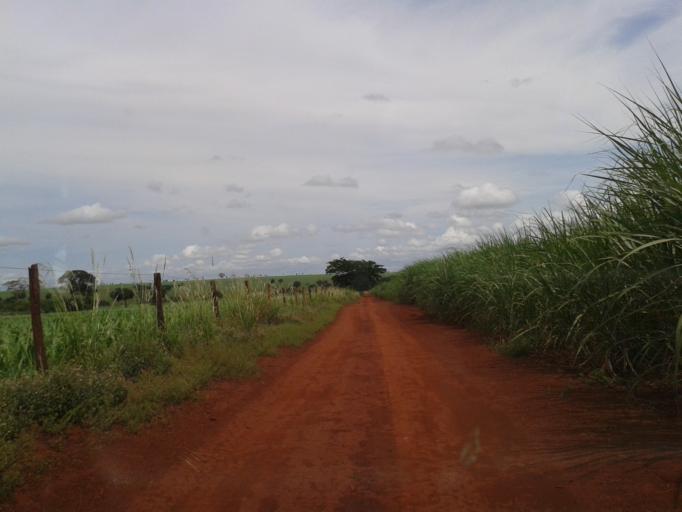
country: BR
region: Minas Gerais
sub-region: Centralina
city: Centralina
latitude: -18.6125
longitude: -49.2874
